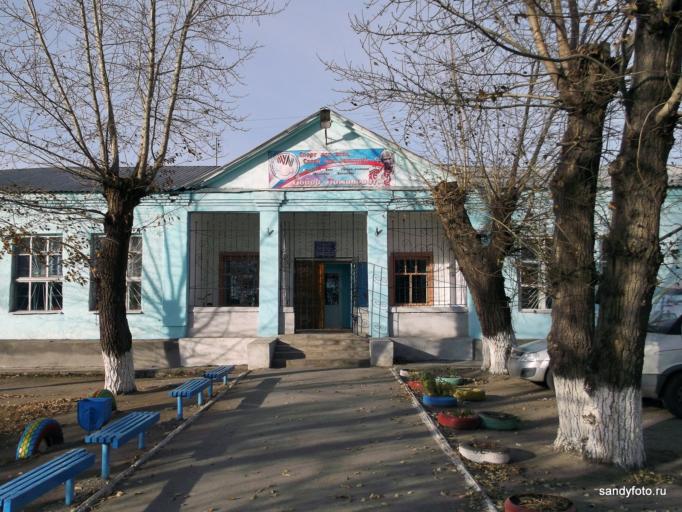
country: RU
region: Chelyabinsk
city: Troitsk
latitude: 54.0958
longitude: 61.5876
